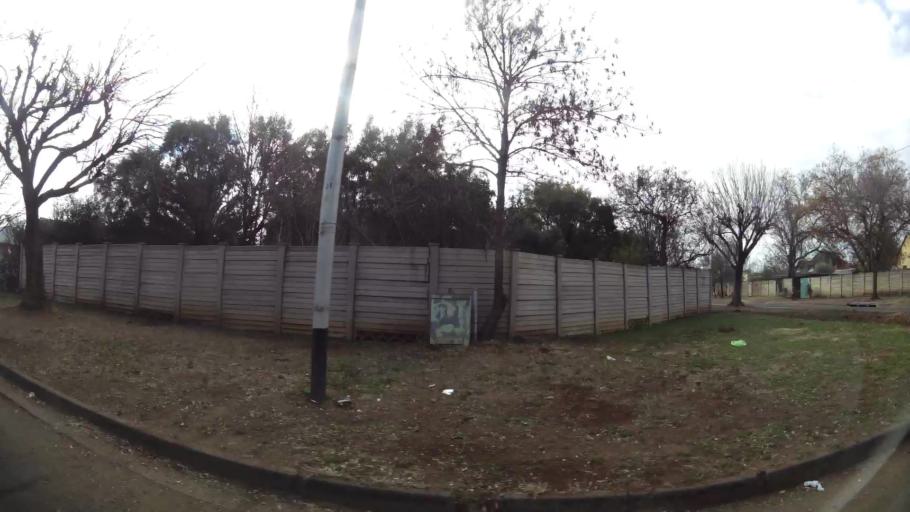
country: ZA
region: Orange Free State
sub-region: Mangaung Metropolitan Municipality
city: Bloemfontein
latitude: -29.0832
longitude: 26.2413
